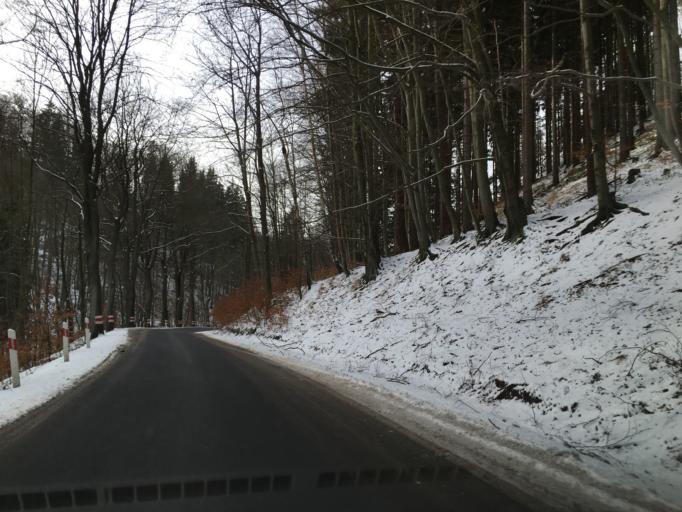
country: PL
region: Lower Silesian Voivodeship
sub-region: Powiat walbrzyski
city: Jedlina-Zdroj
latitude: 50.7042
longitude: 16.3124
